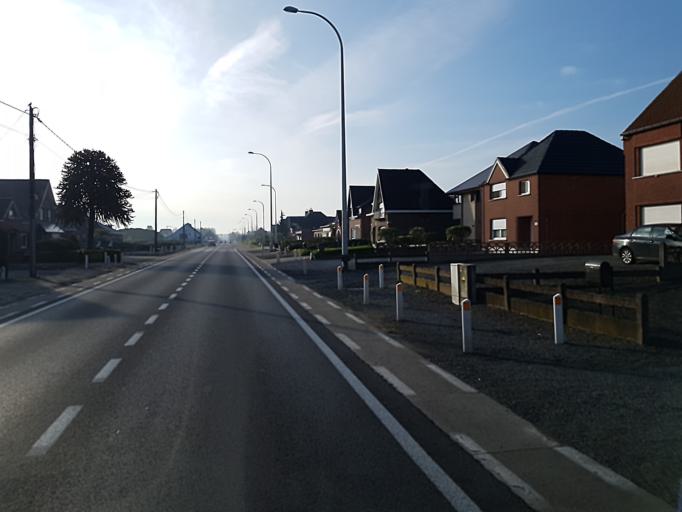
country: BE
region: Flanders
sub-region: Provincie Vlaams-Brabant
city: Begijnendijk
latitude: 51.0233
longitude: 4.7879
